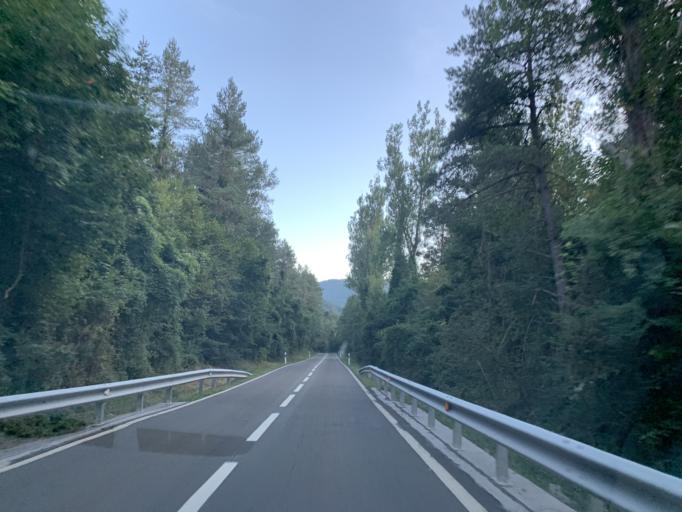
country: ES
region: Aragon
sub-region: Provincia de Huesca
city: Broto
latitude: 42.5639
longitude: -0.1154
